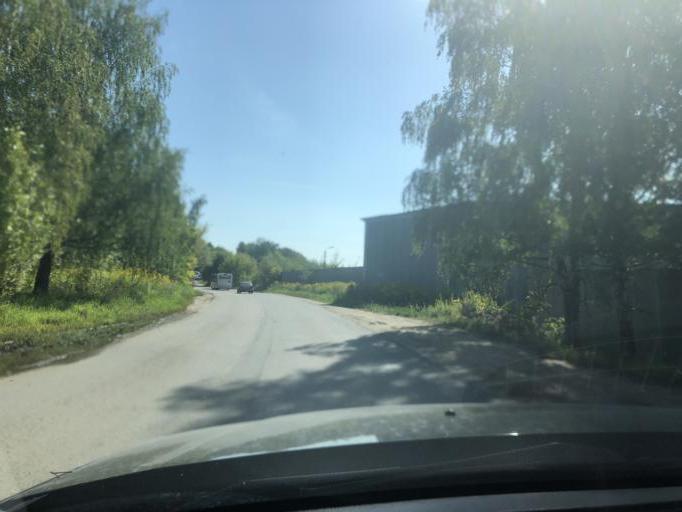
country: RU
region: Tula
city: Skuratovskiy
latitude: 54.1284
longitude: 37.6197
